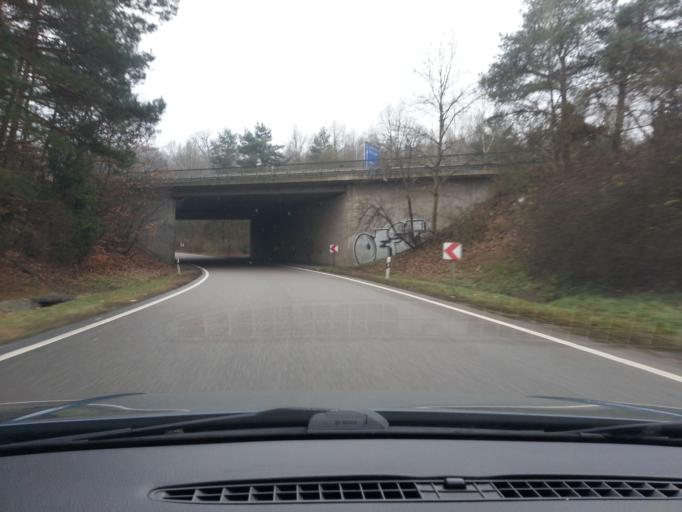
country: DE
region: Saarland
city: Bexbach
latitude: 49.3243
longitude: 7.2345
